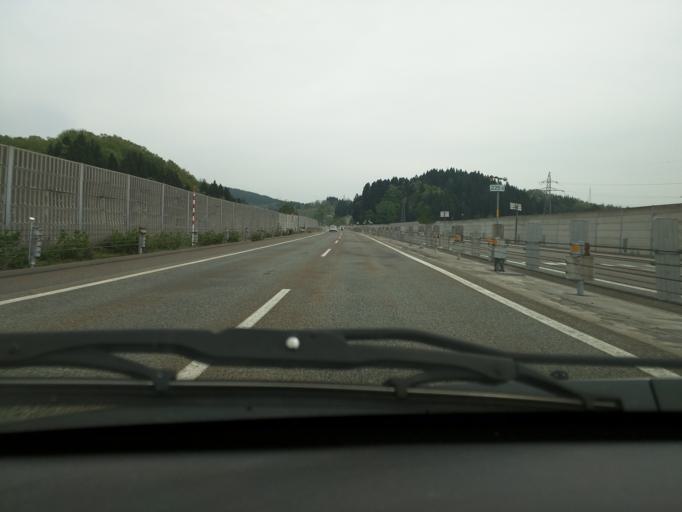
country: JP
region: Niigata
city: Ojiya
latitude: 37.2869
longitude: 138.7851
